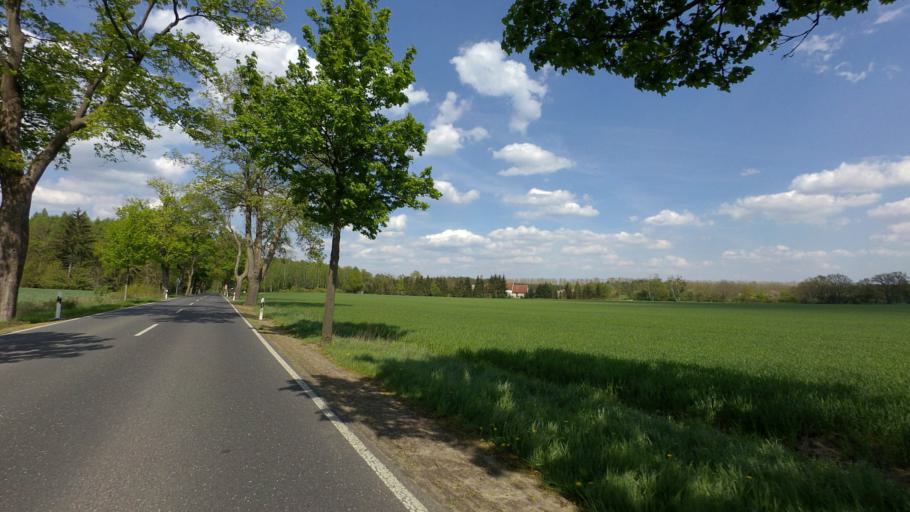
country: DE
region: Brandenburg
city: Marienwerder
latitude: 52.8841
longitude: 13.5449
